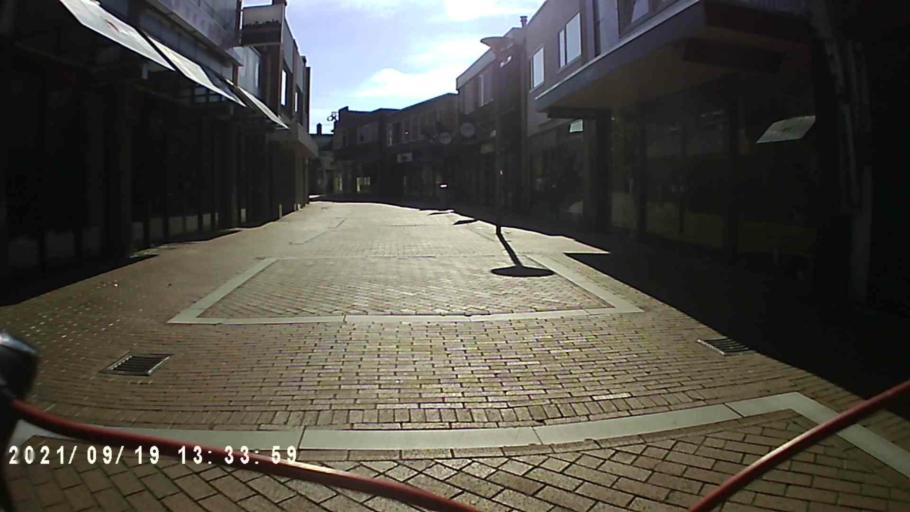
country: NL
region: Groningen
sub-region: Gemeente  Oldambt
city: Winschoten
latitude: 53.1456
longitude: 7.0347
